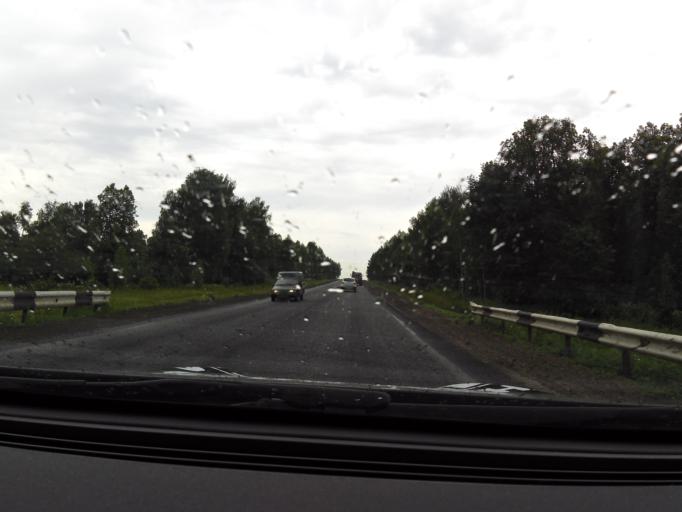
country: RU
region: Bashkortostan
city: Iglino
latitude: 54.7838
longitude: 56.5246
